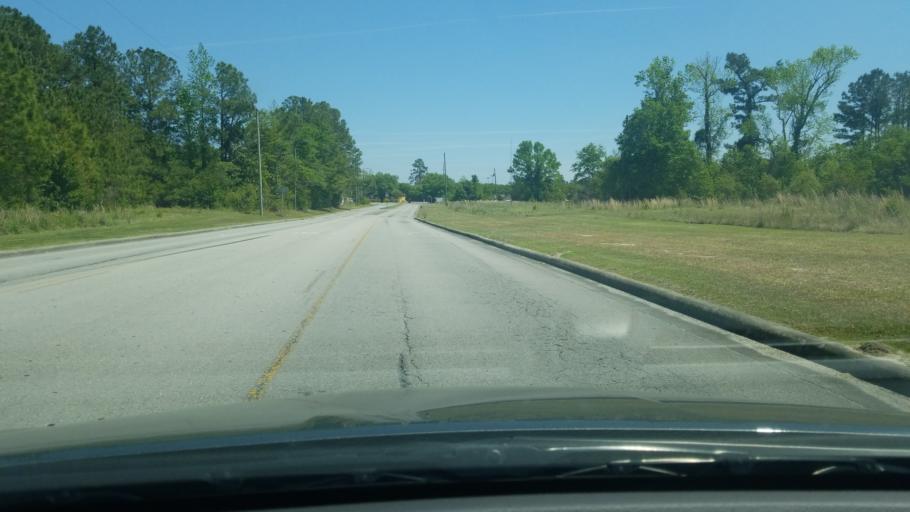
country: US
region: North Carolina
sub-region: Onslow County
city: Jacksonville
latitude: 34.7488
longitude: -77.4583
